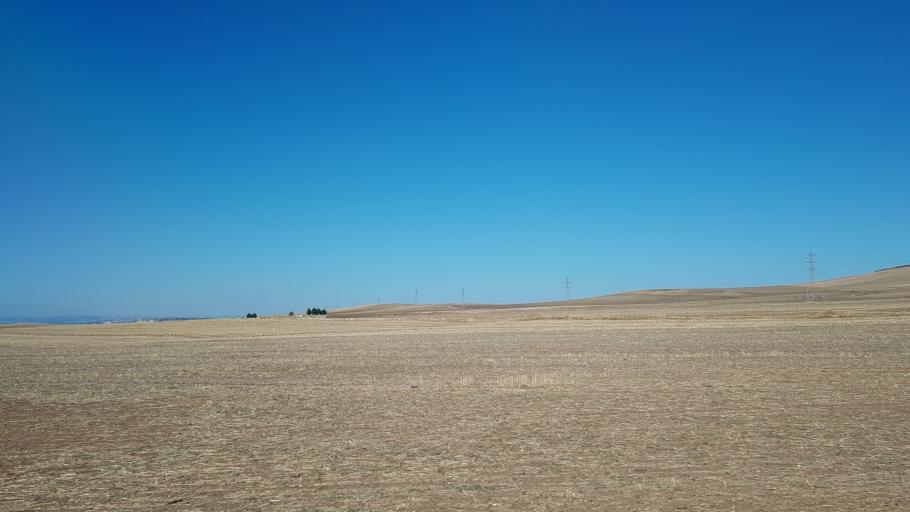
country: TR
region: Tekirdag
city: Corlu
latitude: 41.0223
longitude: 27.8066
